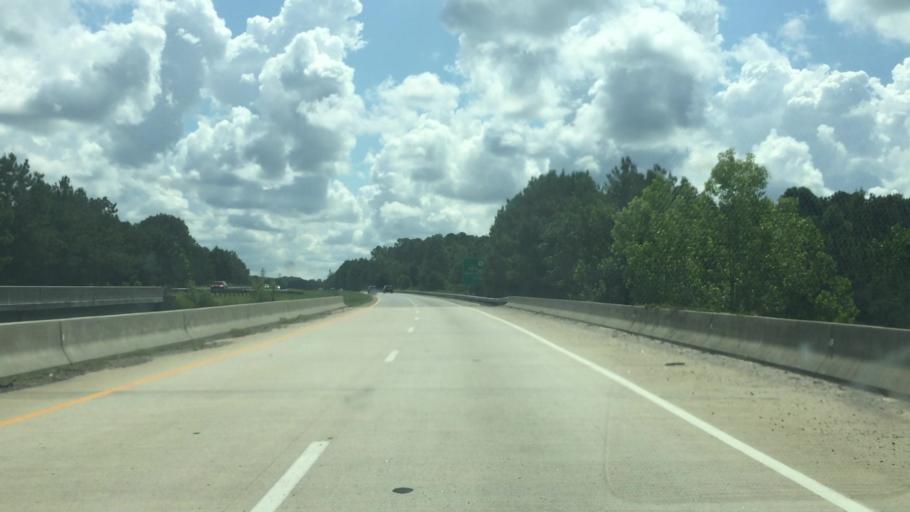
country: US
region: North Carolina
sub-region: Richmond County
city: Cordova
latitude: 34.9210
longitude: -79.8129
